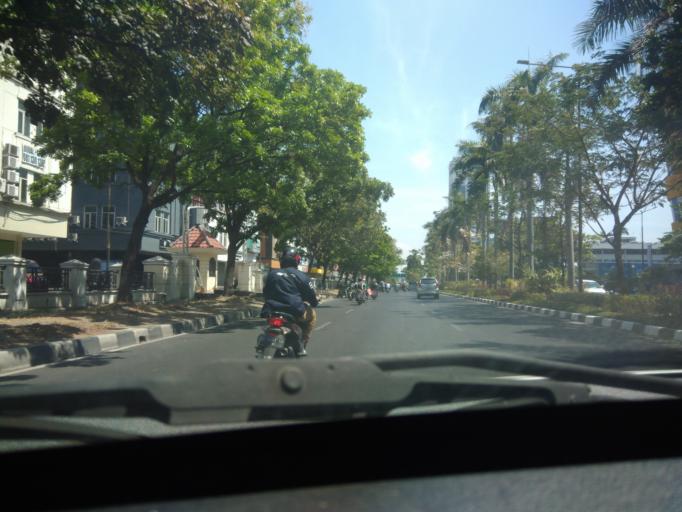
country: ID
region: East Java
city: Mulyorejo
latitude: -7.2848
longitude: 112.7808
